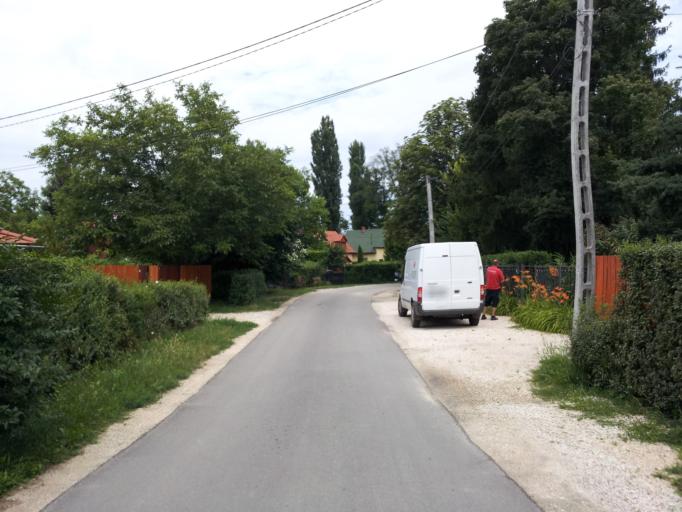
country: HU
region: Pest
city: Szigetujfalu
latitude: 47.2112
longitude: 18.9642
